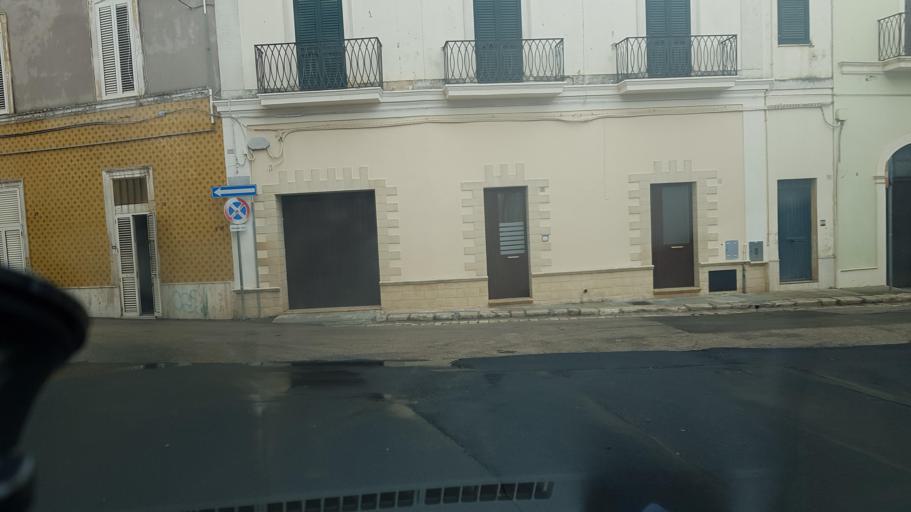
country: IT
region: Apulia
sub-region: Provincia di Lecce
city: Carmiano
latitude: 40.3457
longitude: 18.0470
